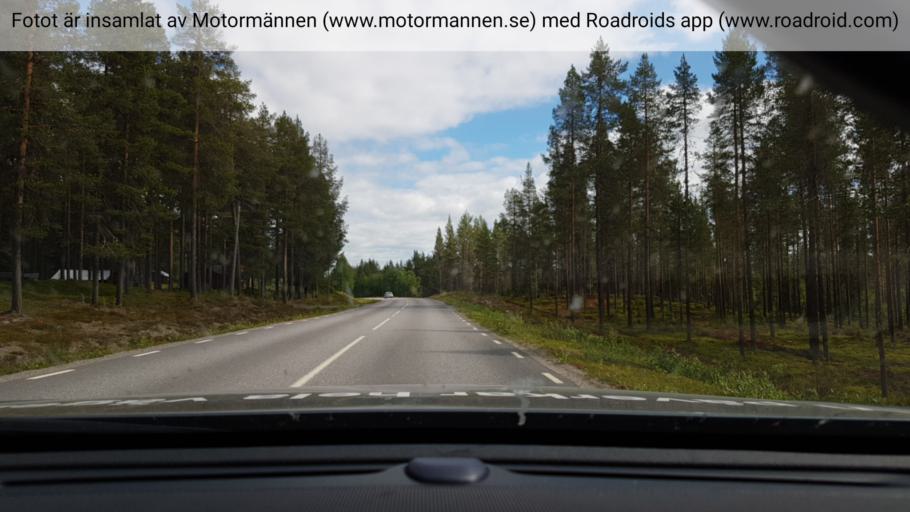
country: SE
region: Vaesterbotten
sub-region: Sorsele Kommun
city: Sorsele
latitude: 65.6901
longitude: 17.2005
